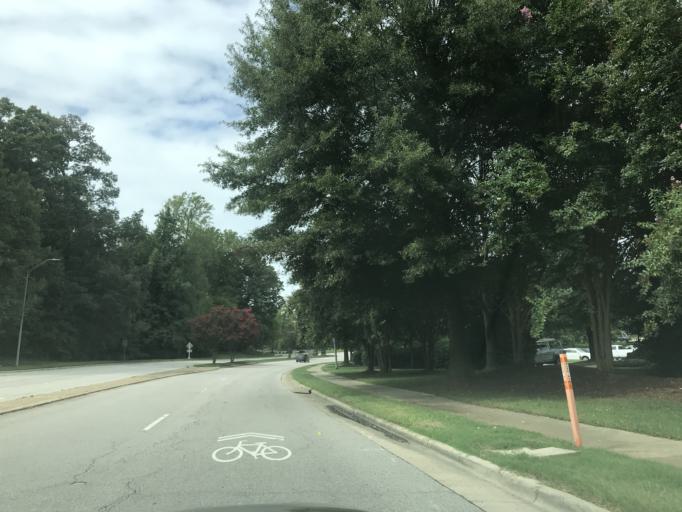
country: US
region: North Carolina
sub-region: Wake County
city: Cary
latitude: 35.7322
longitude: -78.7897
